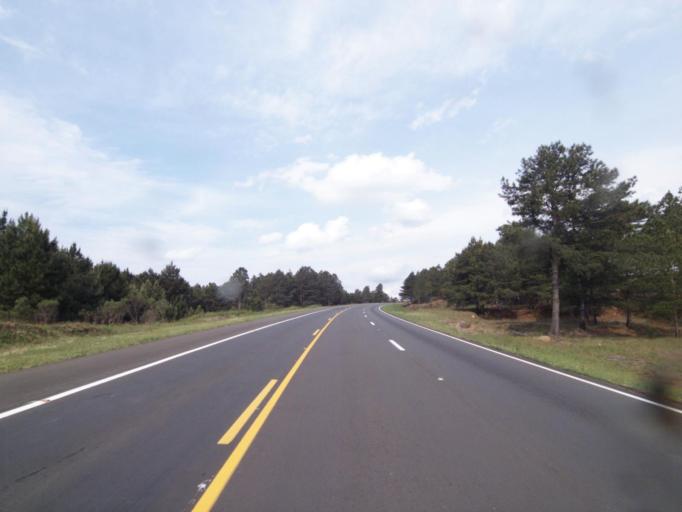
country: BR
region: Parana
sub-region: Campo Largo
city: Campo Largo
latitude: -25.4642
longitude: -49.7601
